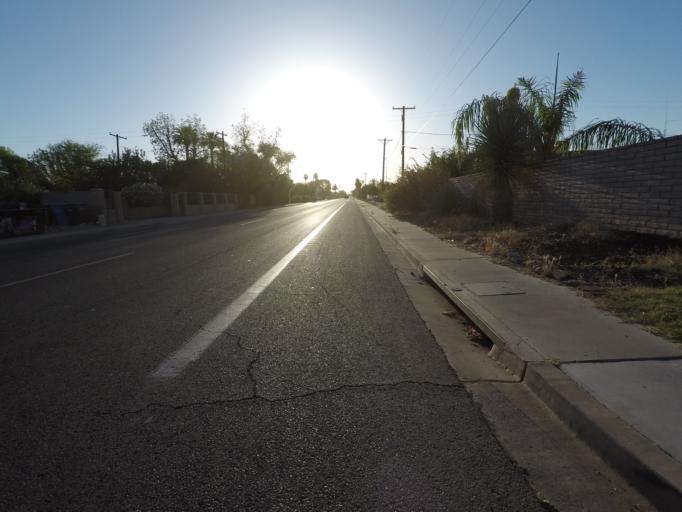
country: US
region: Arizona
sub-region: Maricopa County
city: Phoenix
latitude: 33.4730
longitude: -112.0236
